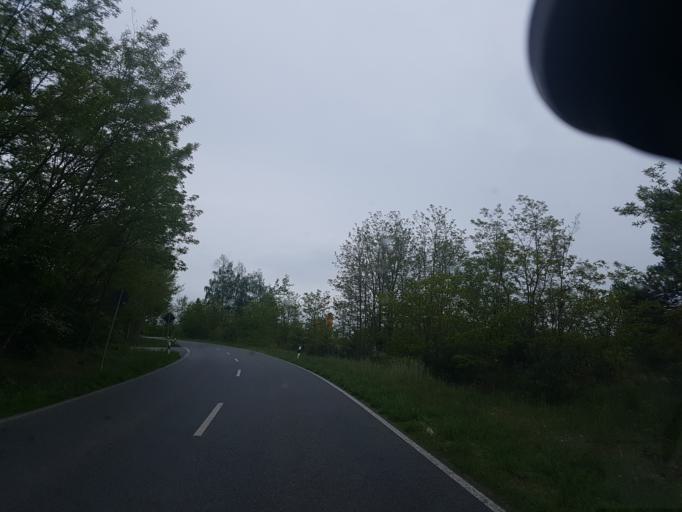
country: DE
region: Brandenburg
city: Grossraschen
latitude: 51.5780
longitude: 13.9738
